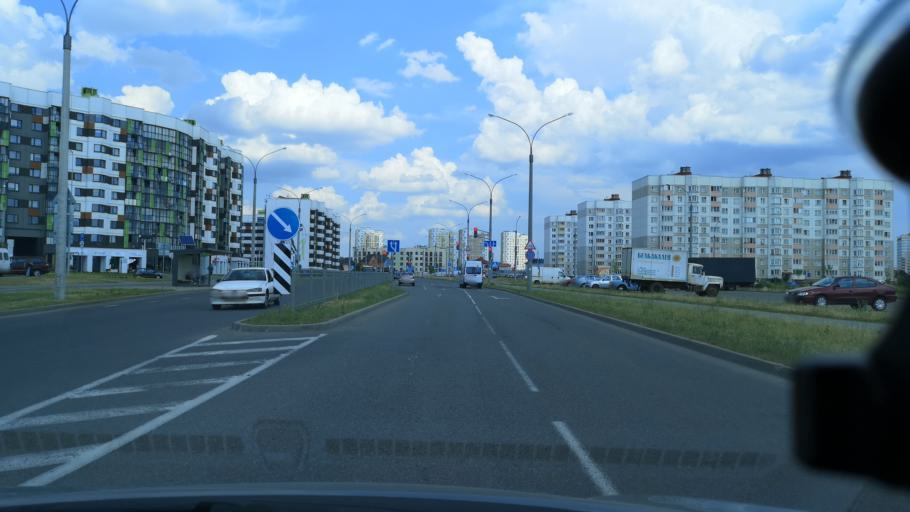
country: BY
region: Minsk
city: Borovlyany
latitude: 53.9514
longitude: 27.6648
